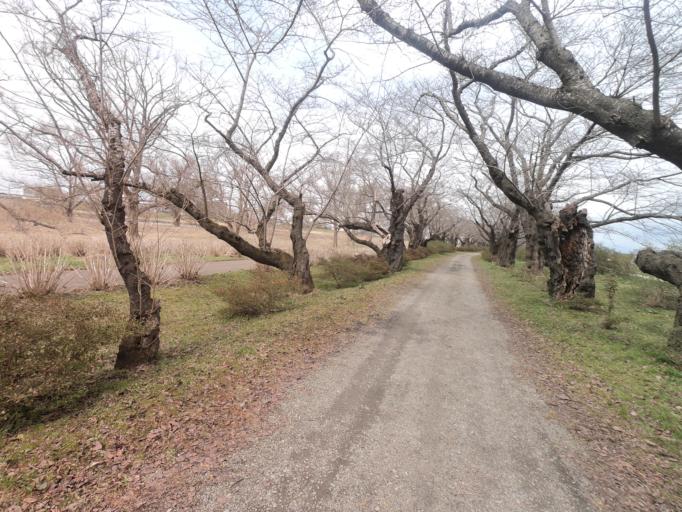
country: JP
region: Iwate
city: Kitakami
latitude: 39.2768
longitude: 141.1270
